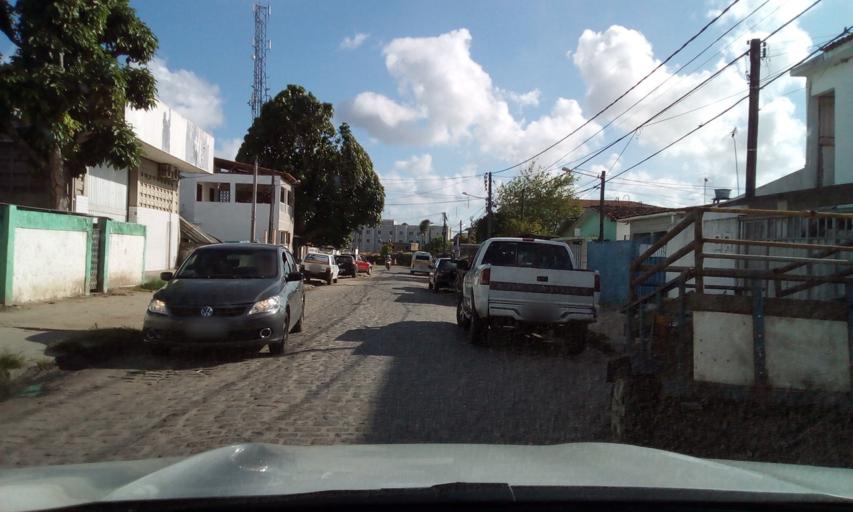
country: BR
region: Paraiba
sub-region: Bayeux
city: Bayeux
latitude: -7.1594
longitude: -34.8969
